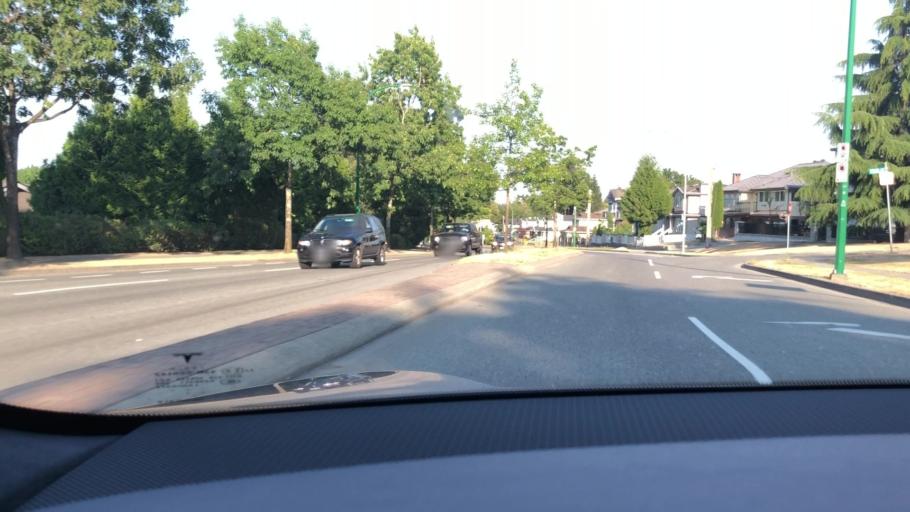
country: CA
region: British Columbia
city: Burnaby
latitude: 49.2299
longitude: -122.9879
